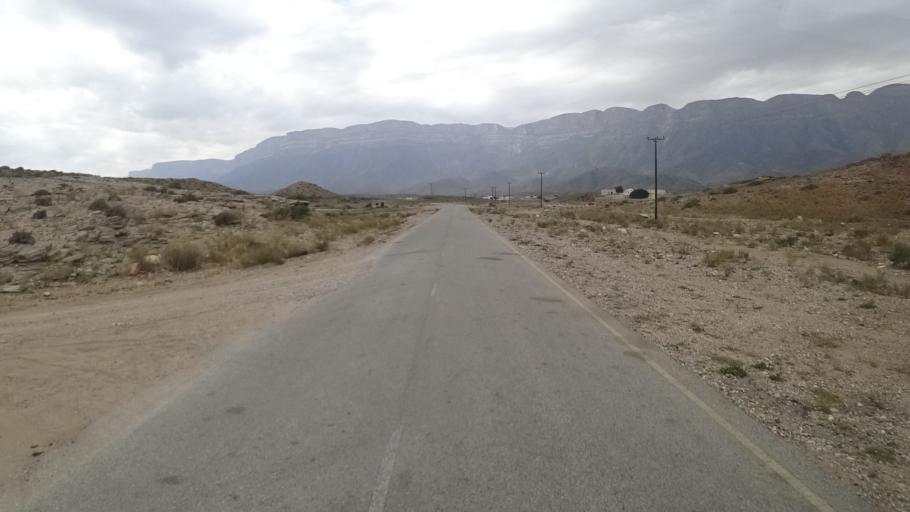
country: OM
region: Zufar
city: Salalah
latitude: 17.1602
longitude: 54.9934
